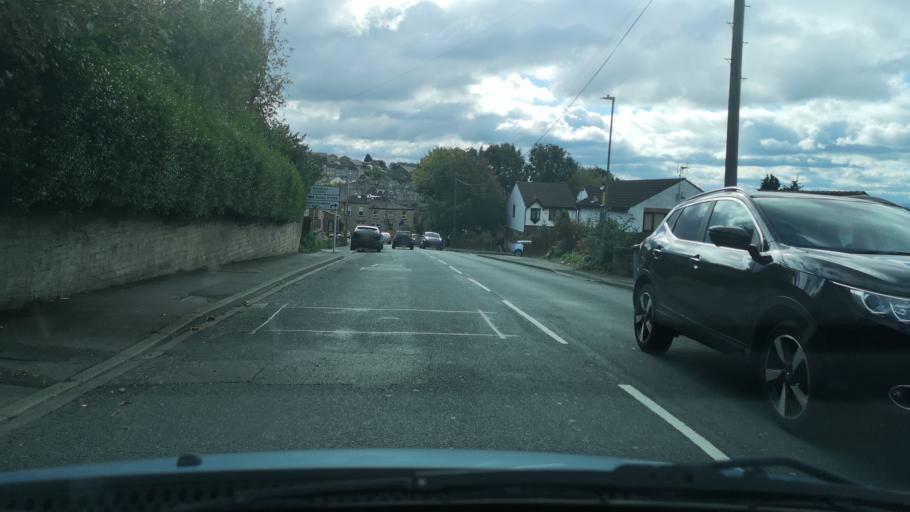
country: GB
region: England
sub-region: Kirklees
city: Heckmondwike
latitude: 53.7119
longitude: -1.6600
